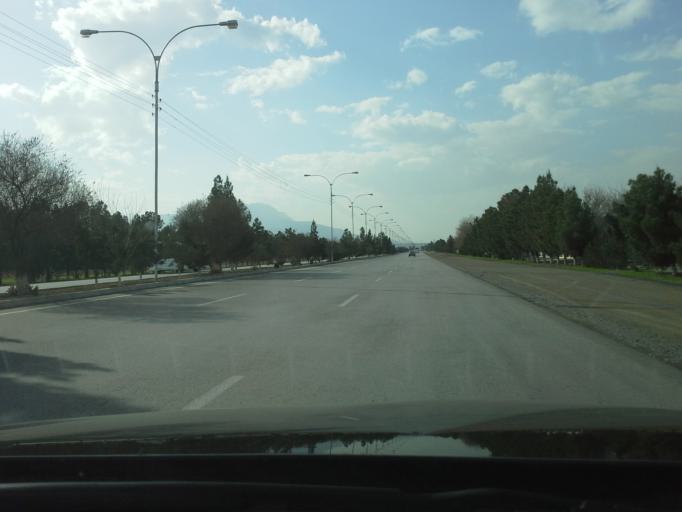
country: TM
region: Ahal
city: Abadan
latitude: 37.9742
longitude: 58.2533
